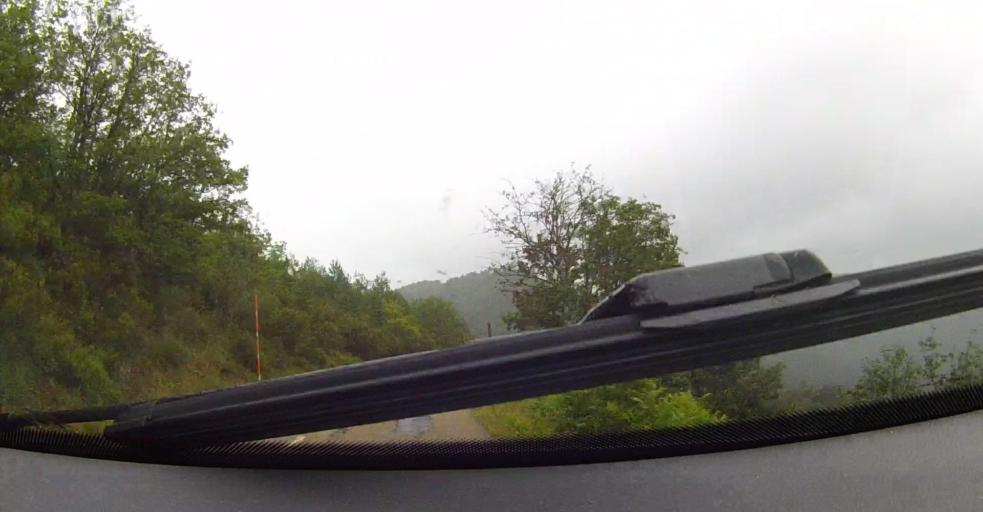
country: ES
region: Castille and Leon
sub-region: Provincia de Leon
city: Puebla de Lillo
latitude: 43.0747
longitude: -5.2650
